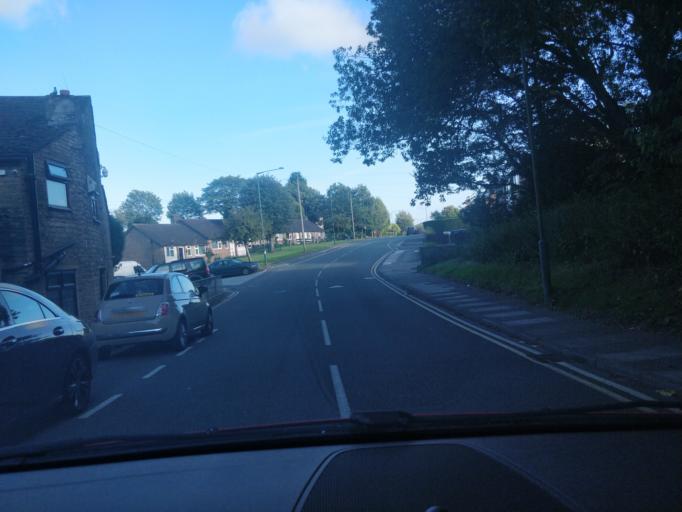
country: GB
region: England
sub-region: St. Helens
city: Billinge
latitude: 53.5340
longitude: -2.7189
